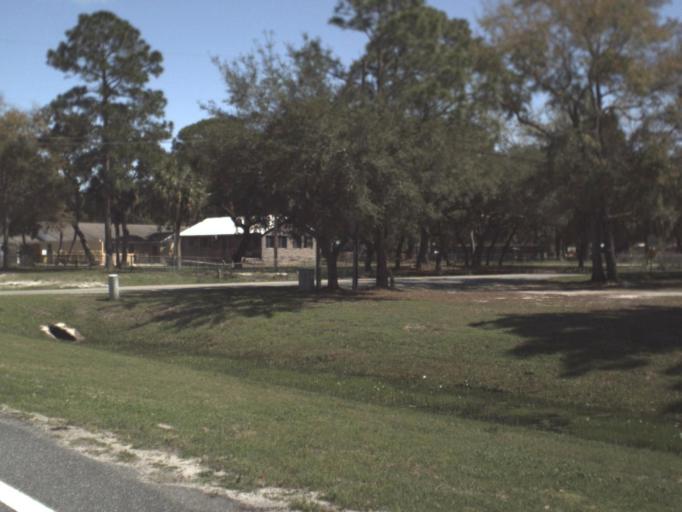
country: US
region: Florida
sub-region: Wakulla County
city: Crawfordville
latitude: 30.0185
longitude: -84.3918
